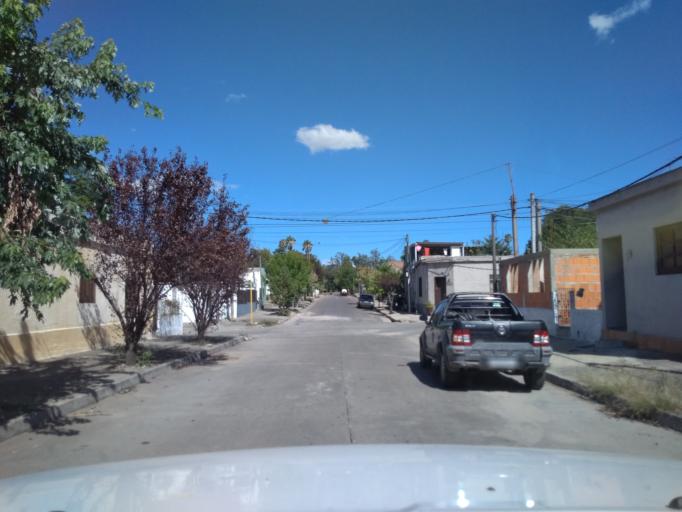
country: UY
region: Florida
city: Florida
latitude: -34.0961
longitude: -56.2090
